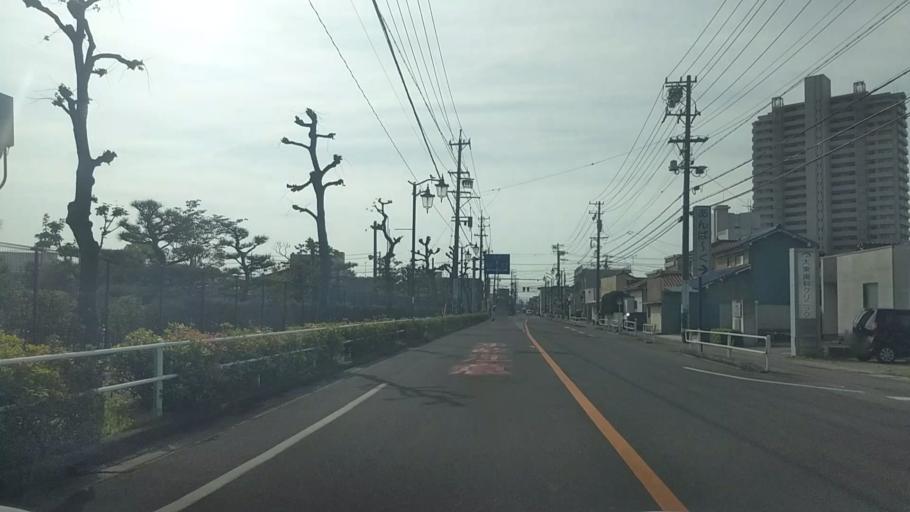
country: JP
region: Aichi
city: Anjo
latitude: 34.9649
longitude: 137.0838
